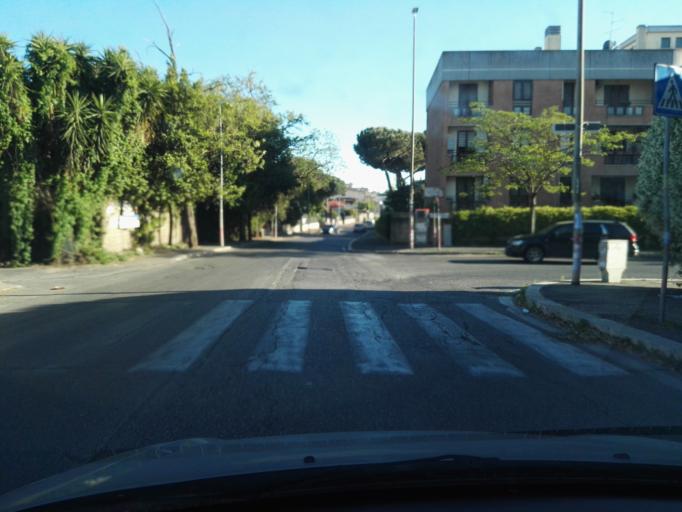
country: IT
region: Latium
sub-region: Citta metropolitana di Roma Capitale
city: Selcetta
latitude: 41.7710
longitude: 12.4795
